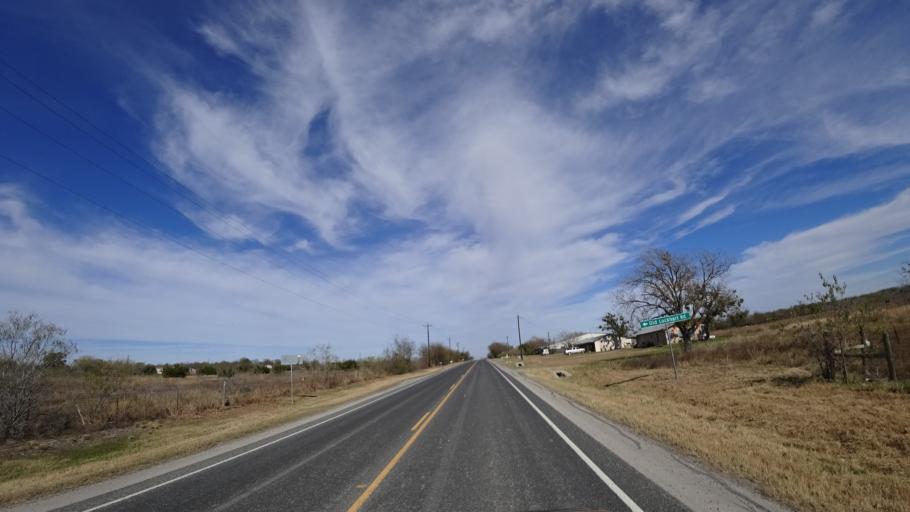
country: US
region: Texas
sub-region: Travis County
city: Onion Creek
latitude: 30.0993
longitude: -97.7287
